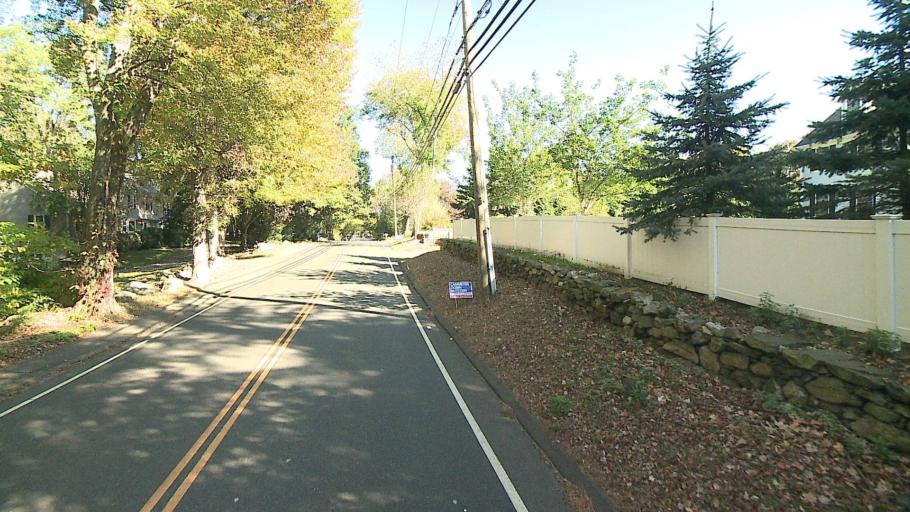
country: US
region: Connecticut
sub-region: Fairfield County
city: Westport
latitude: 41.1737
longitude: -73.3494
